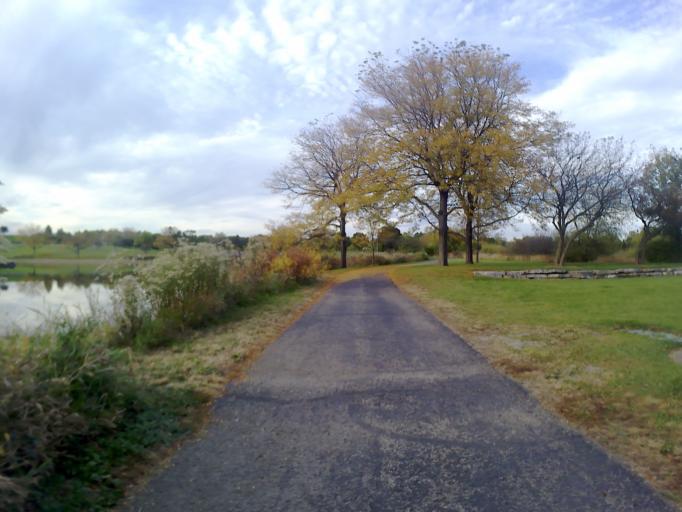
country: US
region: Illinois
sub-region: DuPage County
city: Lisle
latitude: 41.7932
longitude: -88.0796
